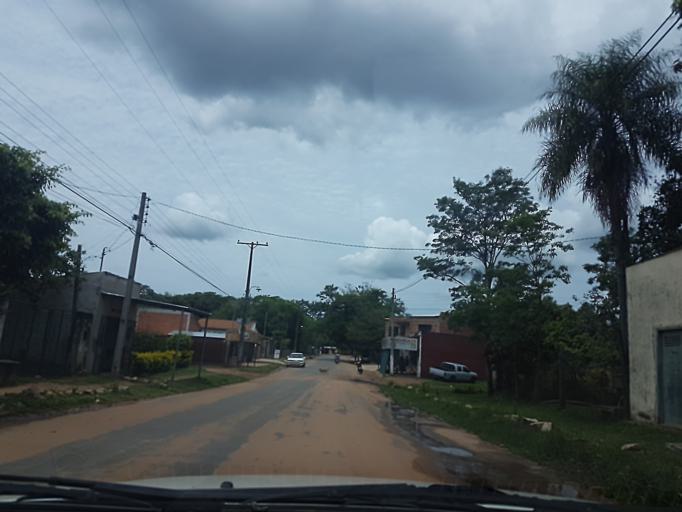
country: PY
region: Central
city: Colonia Mariano Roque Alonso
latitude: -25.1872
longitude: -57.5275
